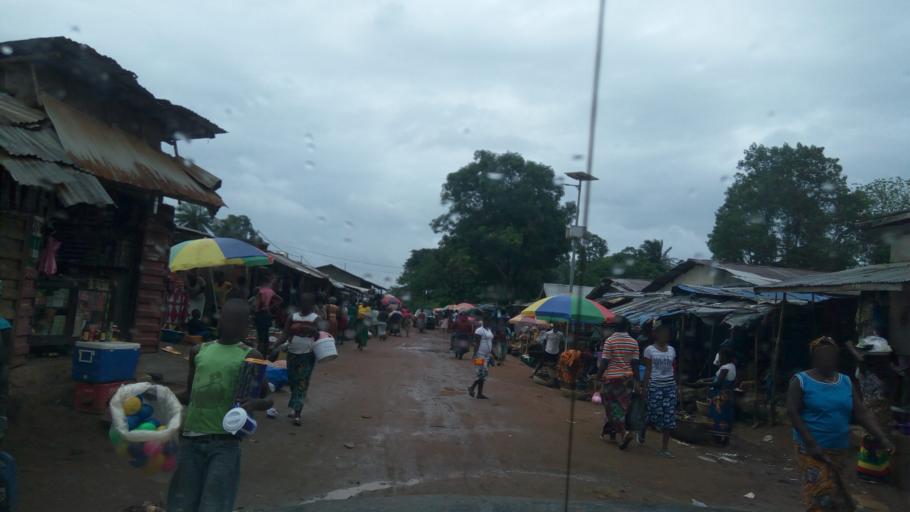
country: SL
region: Northern Province
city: Tintafor
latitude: 8.6282
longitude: -13.2172
